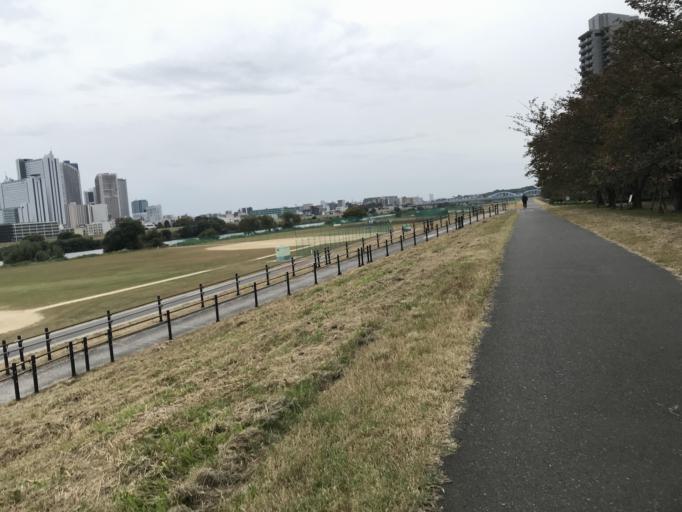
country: JP
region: Kanagawa
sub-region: Kawasaki-shi
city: Kawasaki
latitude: 35.5689
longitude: 139.6779
